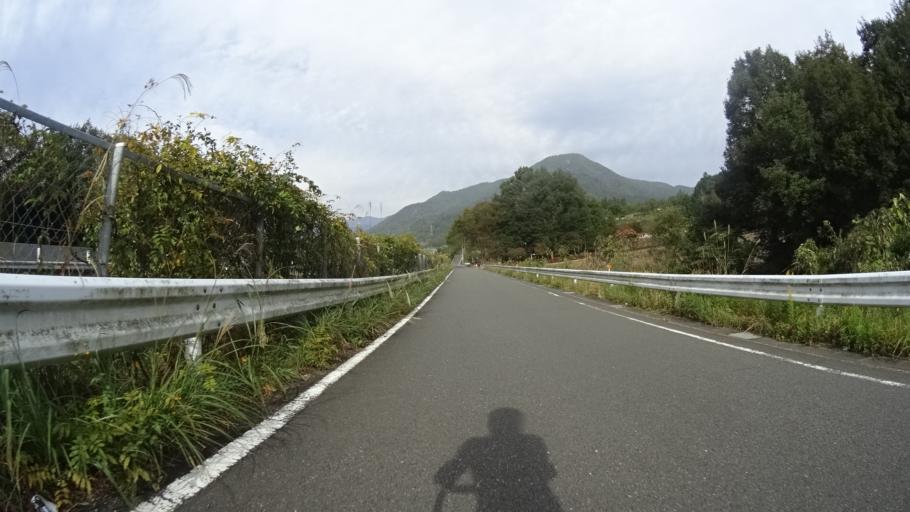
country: JP
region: Yamanashi
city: Otsuki
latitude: 35.6176
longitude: 138.9970
